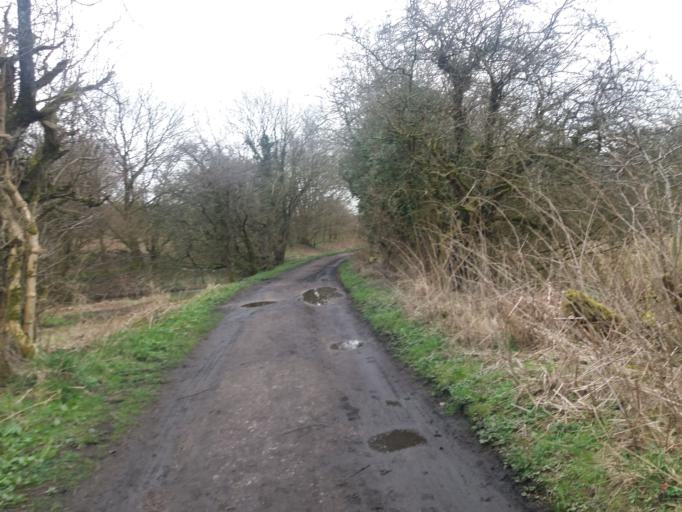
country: GB
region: England
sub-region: Lancashire
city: Chorley
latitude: 53.6608
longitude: -2.6101
